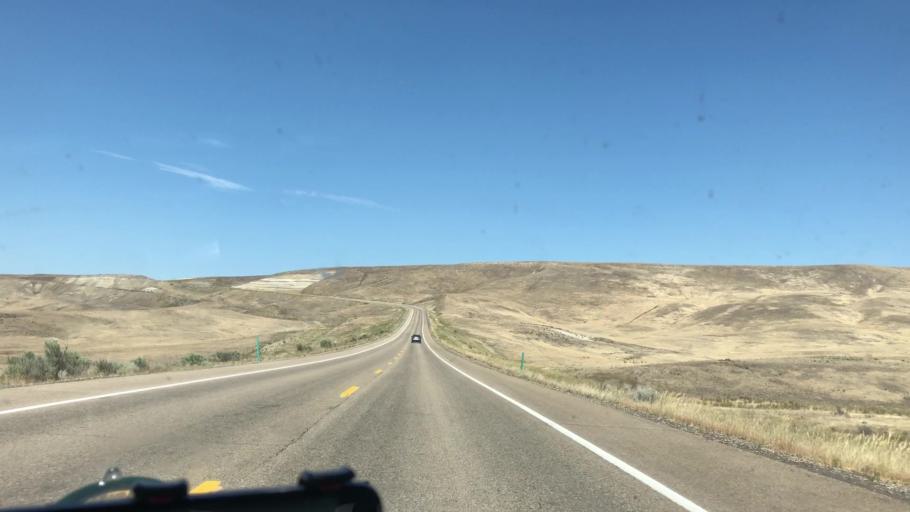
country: US
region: Idaho
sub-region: Owyhee County
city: Marsing
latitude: 43.2807
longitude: -116.9930
